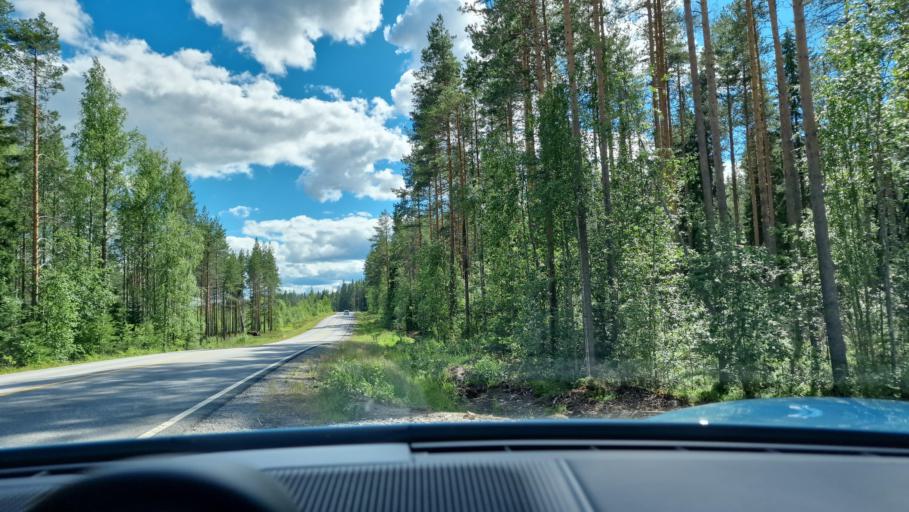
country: FI
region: Central Finland
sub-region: Saarijaervi-Viitasaari
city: Pylkoenmaeki
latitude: 62.6517
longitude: 24.5721
